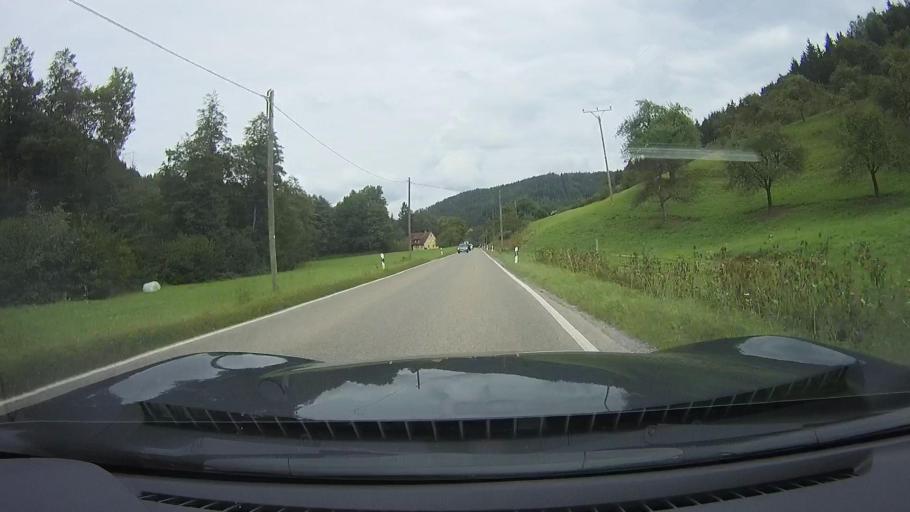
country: DE
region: Baden-Wuerttemberg
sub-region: Regierungsbezirk Stuttgart
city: Kaisersbach
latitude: 48.9576
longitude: 9.6397
